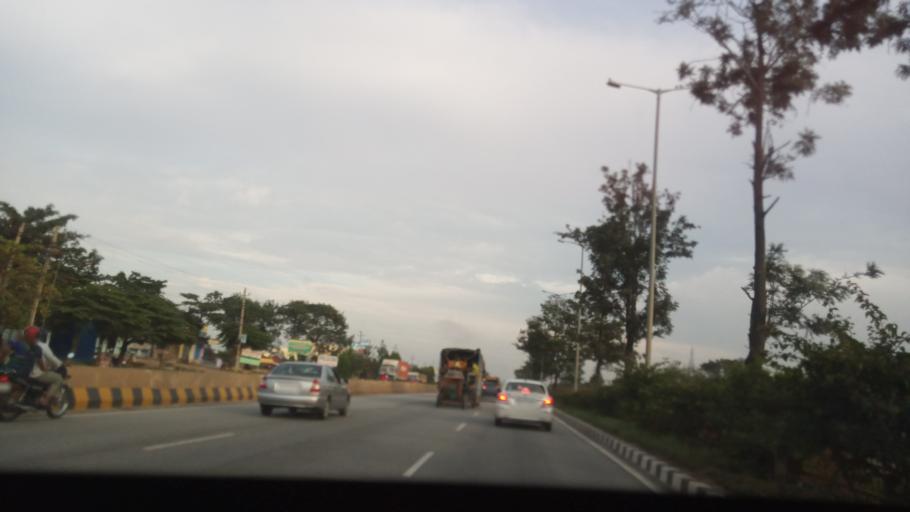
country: IN
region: Karnataka
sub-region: Bangalore Rural
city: Nelamangala
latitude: 13.0878
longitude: 77.4067
